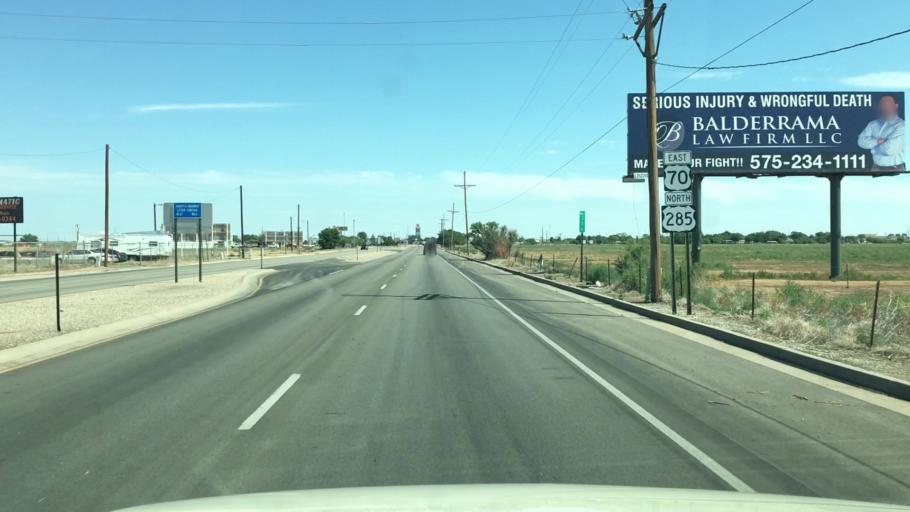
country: US
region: New Mexico
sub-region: Chaves County
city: Roswell
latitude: 33.4532
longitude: -104.5233
